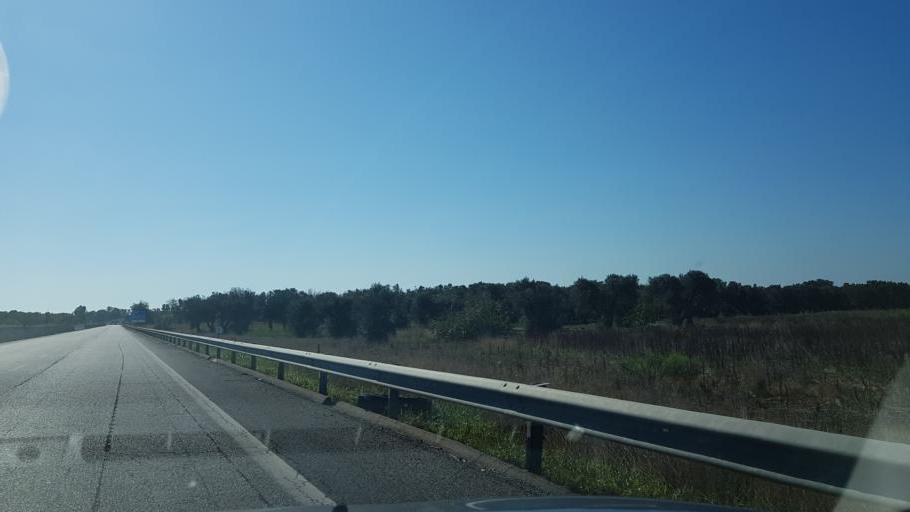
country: IT
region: Apulia
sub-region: Provincia di Brindisi
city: San Pietro Vernotico
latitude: 40.5294
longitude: 18.0112
